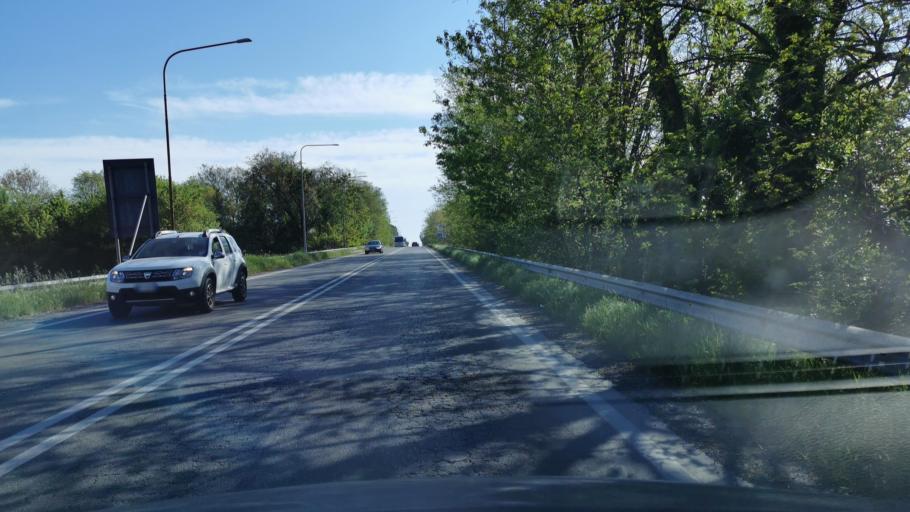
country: IT
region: Lombardy
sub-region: Provincia di Cremona
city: Cremona
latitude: 45.1388
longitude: 10.0458
